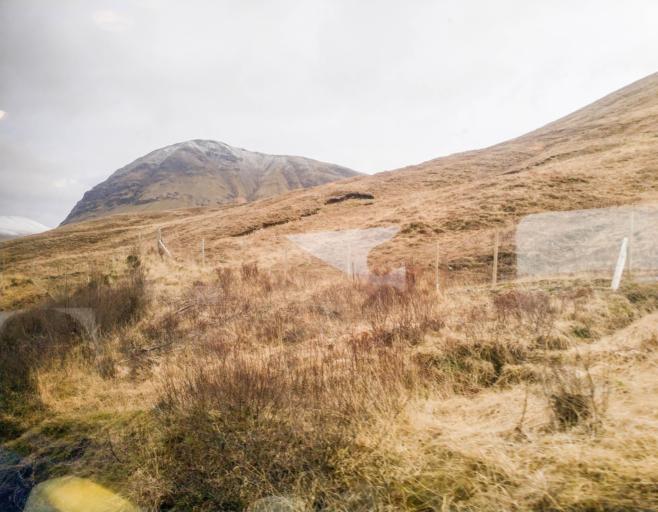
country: GB
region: Scotland
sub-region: Argyll and Bute
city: Garelochhead
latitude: 56.4770
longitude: -4.7170
